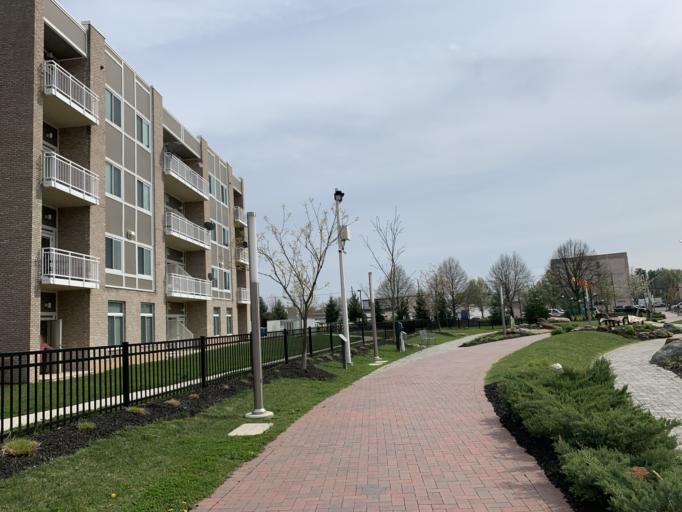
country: US
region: Maryland
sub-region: Washington County
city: Hagerstown
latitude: 39.6387
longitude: -77.7247
